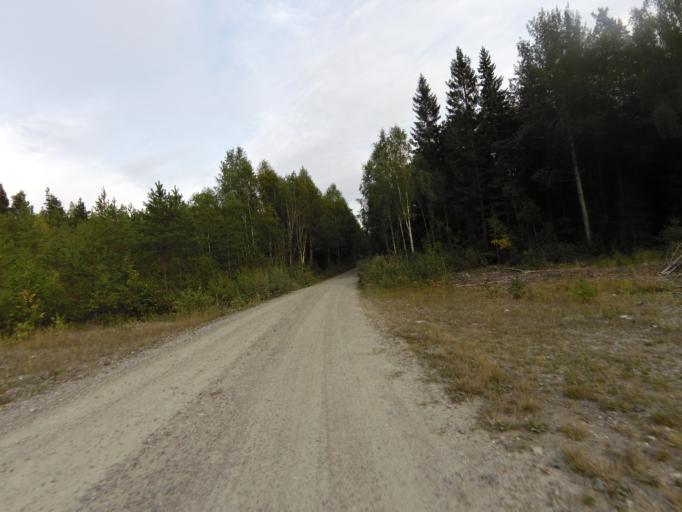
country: SE
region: Gaevleborg
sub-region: Gavle Kommun
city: Gavle
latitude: 60.7103
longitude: 17.1125
